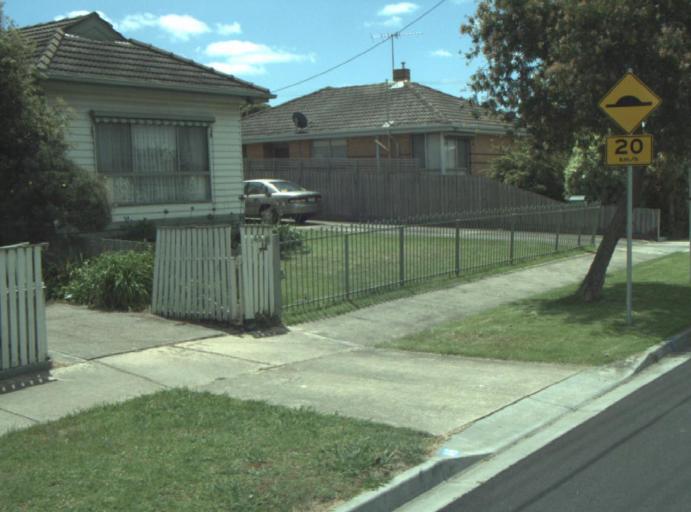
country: AU
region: Victoria
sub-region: Greater Geelong
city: Breakwater
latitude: -38.1849
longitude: 144.3499
